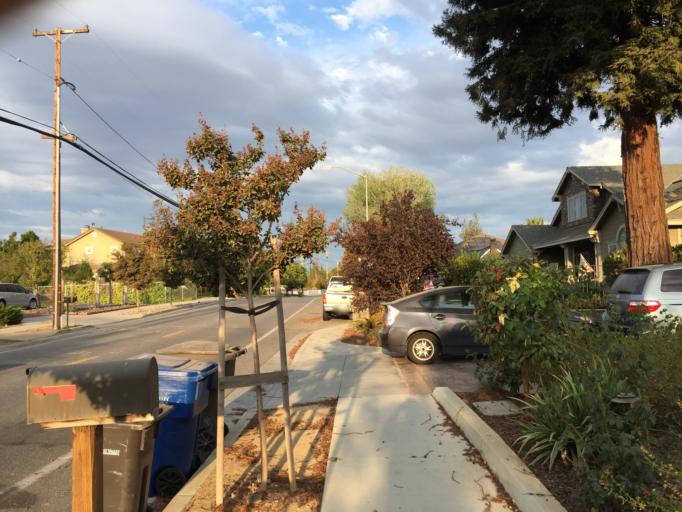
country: US
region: California
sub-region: Santa Clara County
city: Campbell
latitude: 37.2718
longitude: -121.9751
